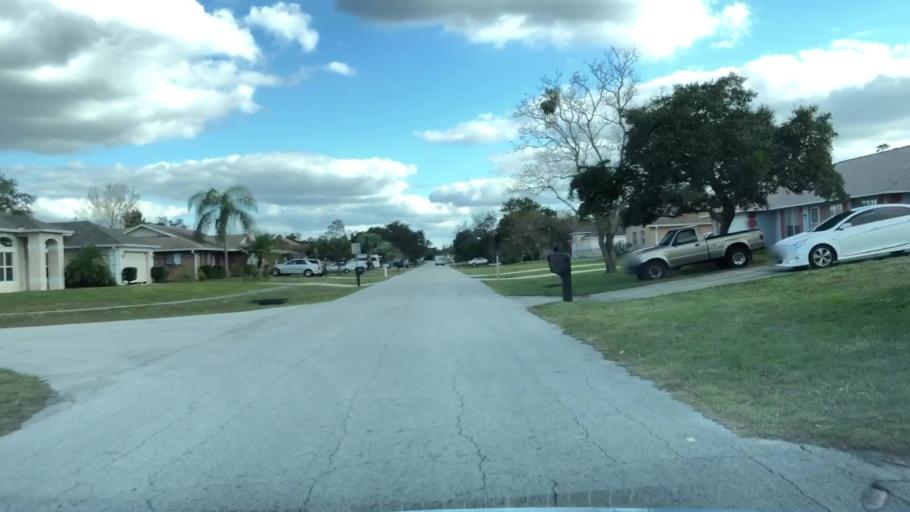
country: US
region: Florida
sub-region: Volusia County
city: Deltona
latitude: 28.8798
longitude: -81.2400
